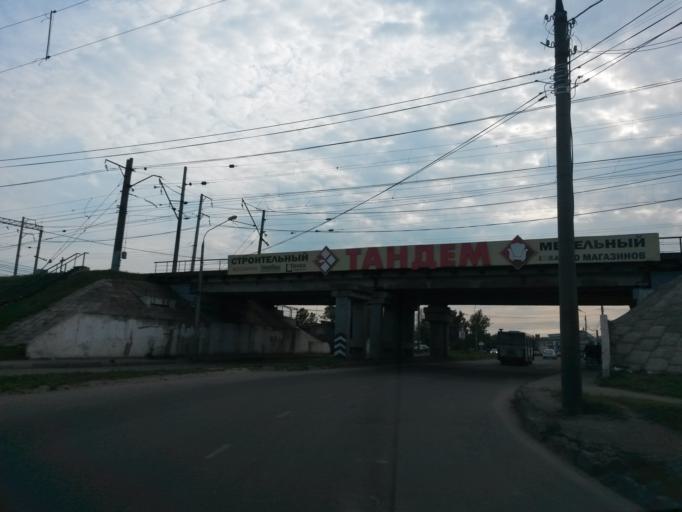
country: RU
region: Jaroslavl
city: Yaroslavl
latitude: 57.6183
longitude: 39.8481
